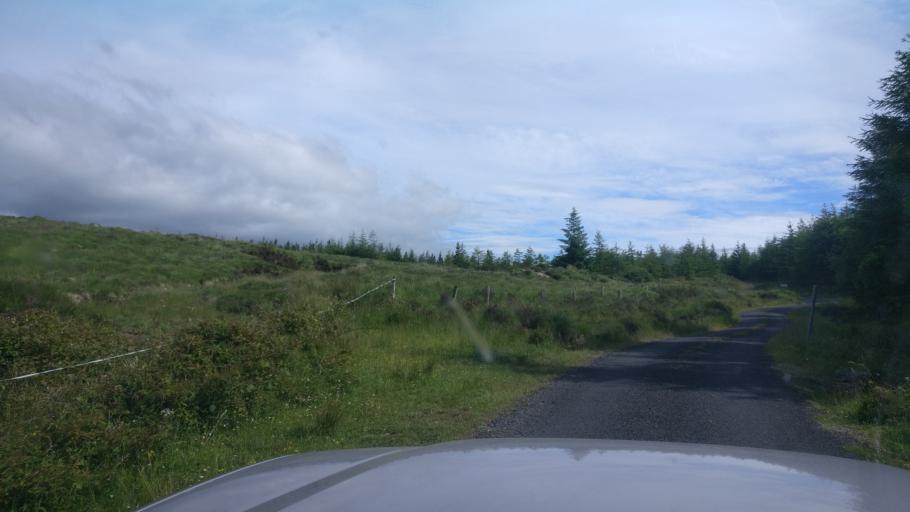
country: IE
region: Connaught
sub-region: County Galway
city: Gort
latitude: 53.0863
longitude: -8.6933
